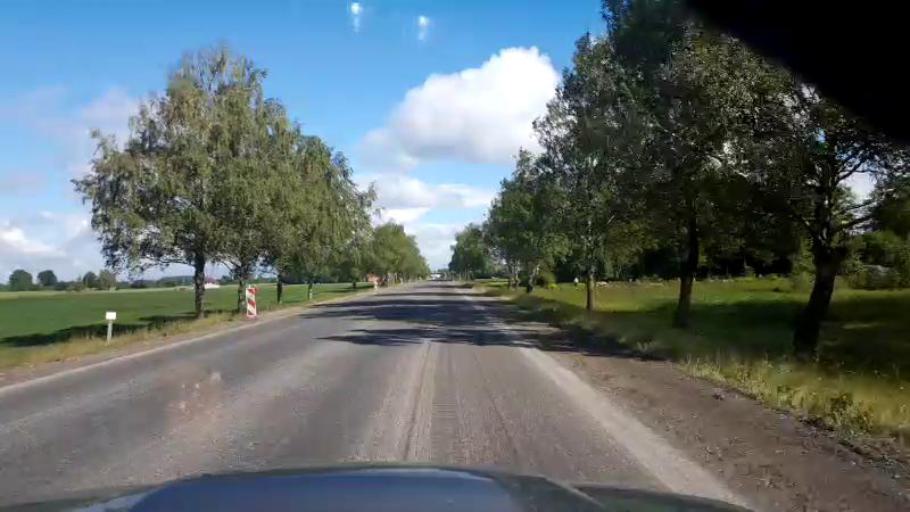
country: LV
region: Bauskas Rajons
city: Bauska
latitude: 56.3571
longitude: 24.2845
